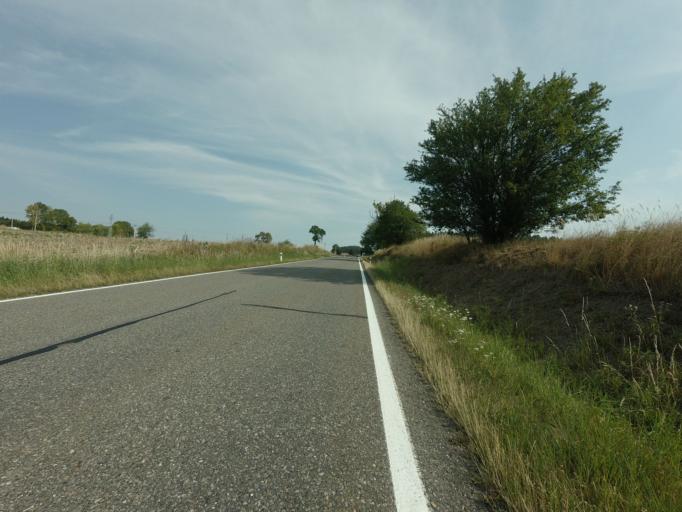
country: CZ
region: Jihocesky
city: Milevsko
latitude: 49.5001
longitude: 14.3628
